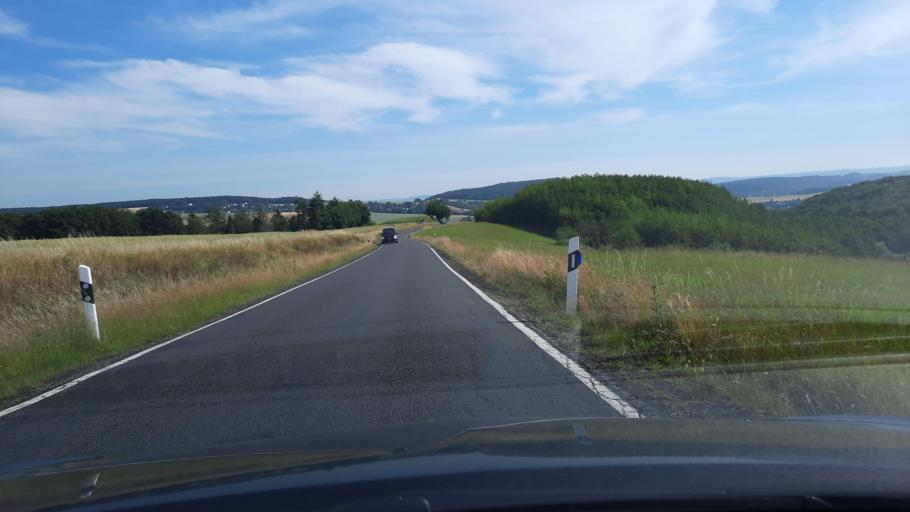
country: DE
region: Rheinland-Pfalz
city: Oberzissen
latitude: 50.4477
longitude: 7.1987
